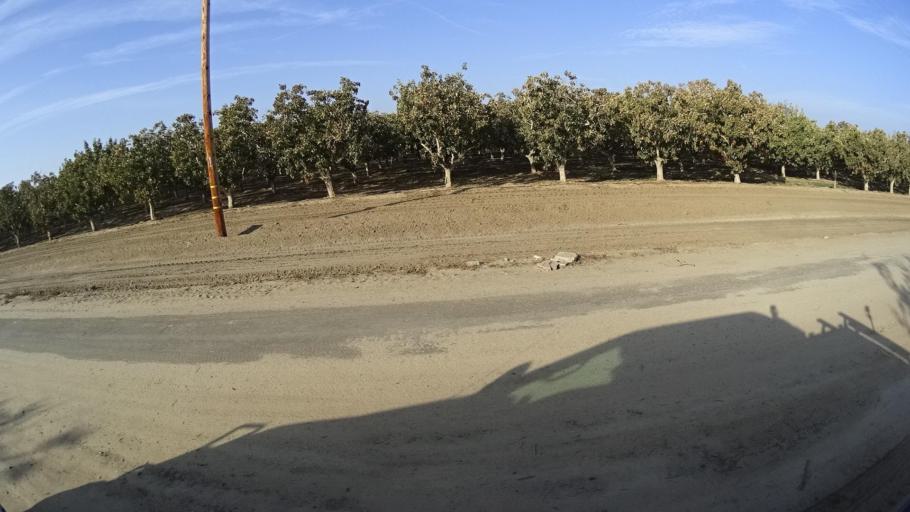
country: US
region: California
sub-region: Kern County
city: McFarland
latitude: 35.7234
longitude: -119.1872
